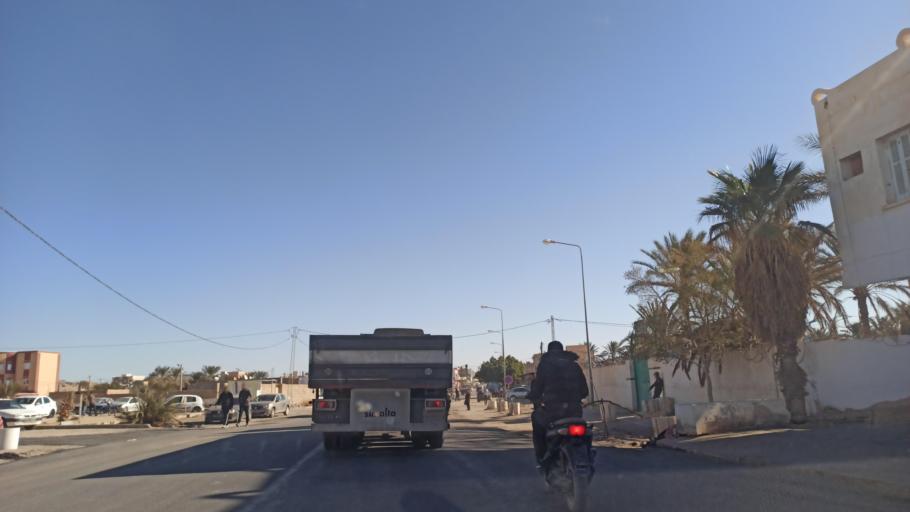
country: TN
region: Gafsa
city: Al Metlaoui
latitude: 34.3162
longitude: 8.3973
